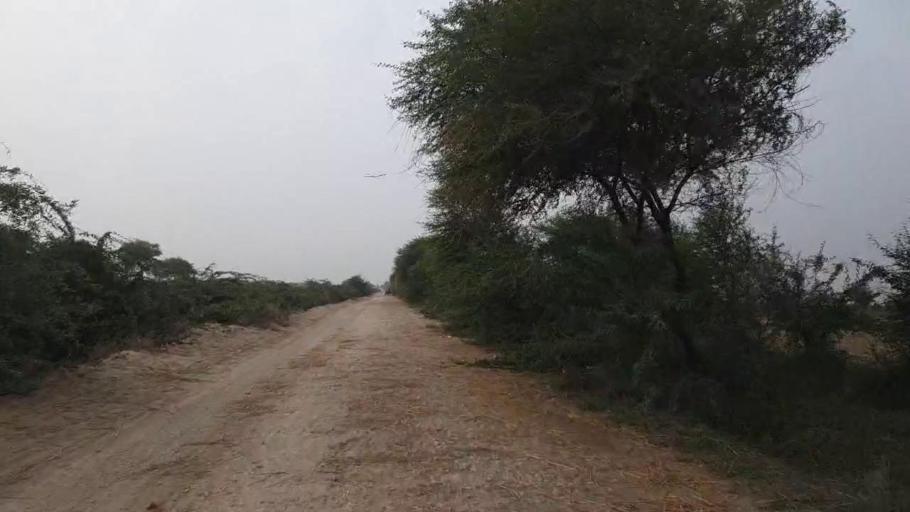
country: PK
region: Sindh
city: Kario
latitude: 24.9051
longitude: 68.5329
